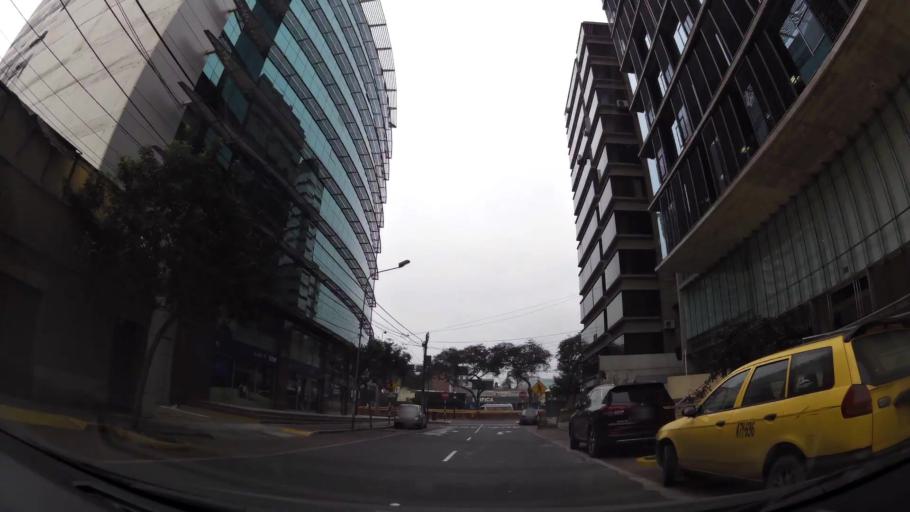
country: PE
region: Lima
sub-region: Lima
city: San Isidro
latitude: -12.1196
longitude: -77.0337
